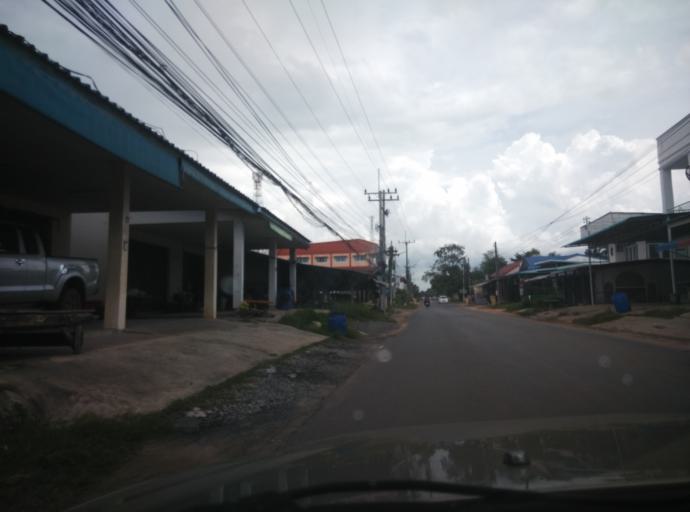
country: TH
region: Sisaket
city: Huai Thap Than
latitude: 15.0529
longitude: 104.0311
